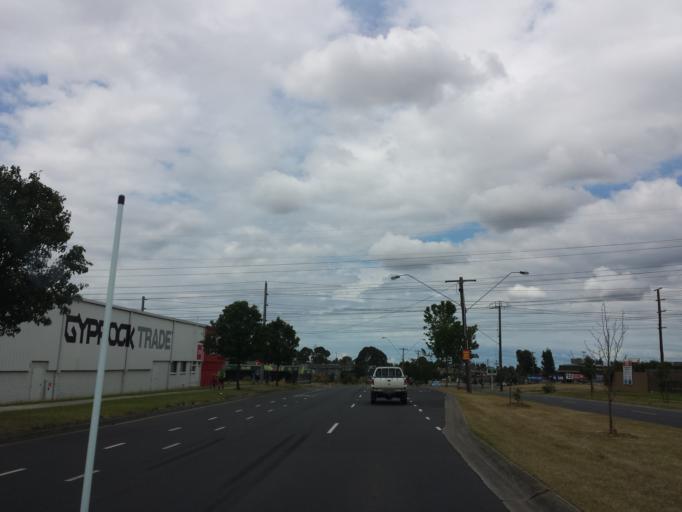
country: AU
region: Victoria
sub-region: Whittlesea
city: Thomastown
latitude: -37.6910
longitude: 145.0022
